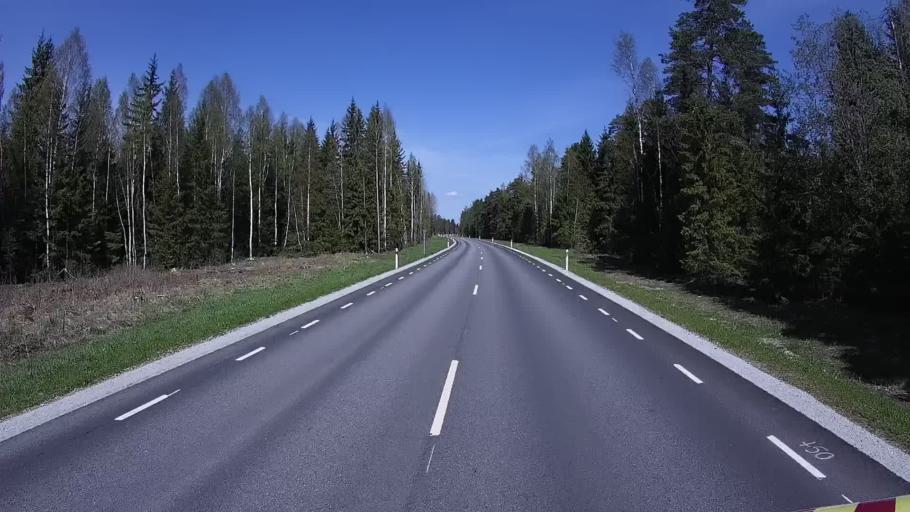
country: EE
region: Harju
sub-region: Nissi vald
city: Turba
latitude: 59.1361
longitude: 24.0745
